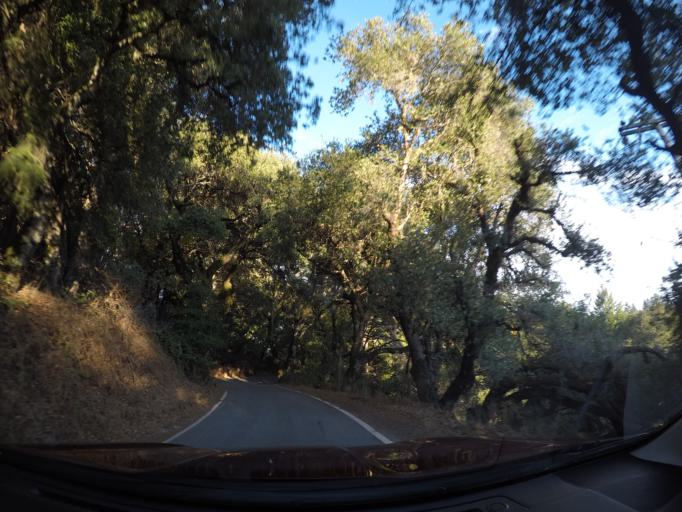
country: US
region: California
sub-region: Santa Clara County
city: Lexington Hills
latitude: 37.1583
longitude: -122.0033
